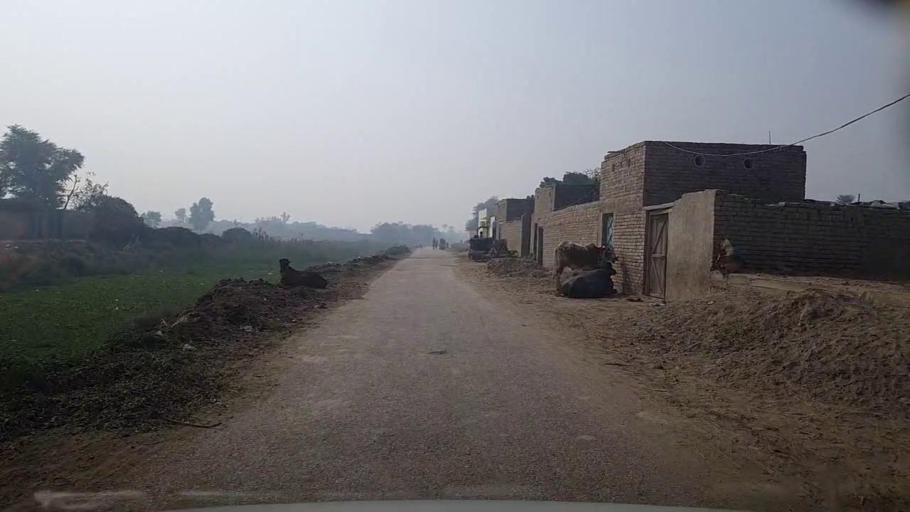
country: PK
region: Sindh
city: Setharja Old
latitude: 27.1970
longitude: 68.4809
